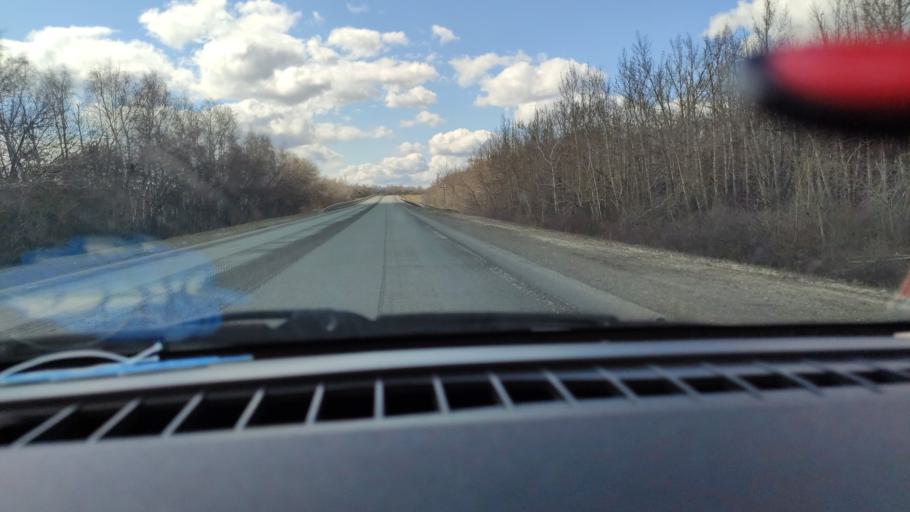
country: RU
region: Saratov
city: Dukhovnitskoye
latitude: 52.6243
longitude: 48.1776
